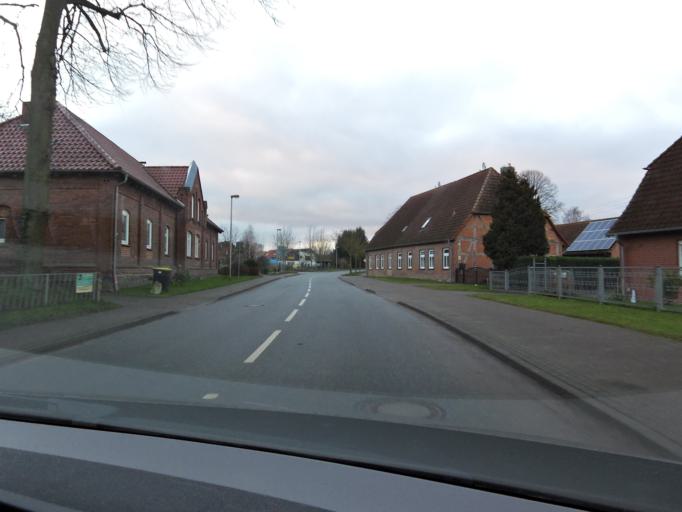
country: DE
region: Mecklenburg-Vorpommern
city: Roggendorf
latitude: 53.6943
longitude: 11.0134
